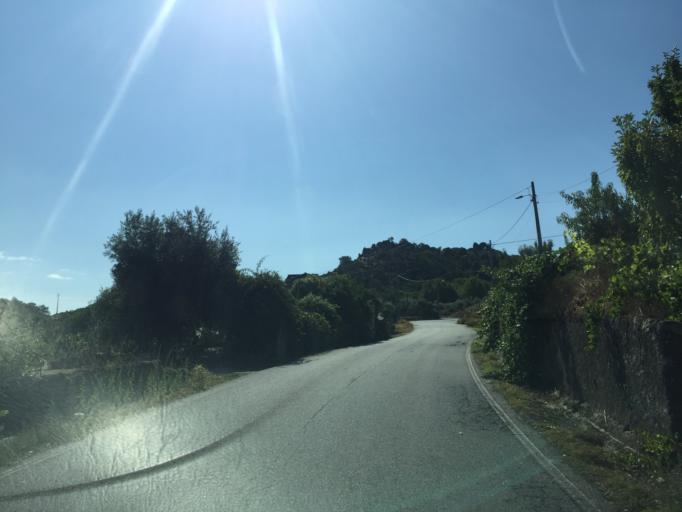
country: PT
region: Portalegre
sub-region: Marvao
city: Marvao
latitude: 39.4006
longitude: -7.3704
